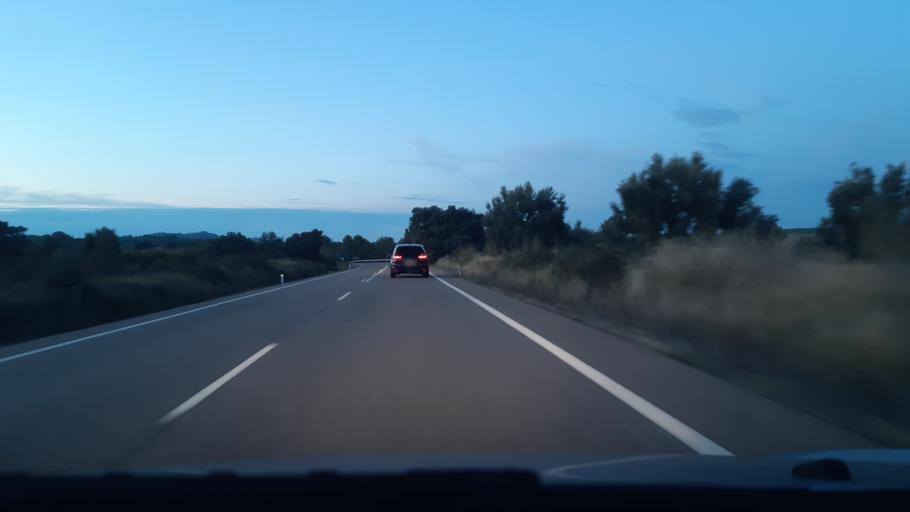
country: ES
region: Aragon
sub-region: Provincia de Teruel
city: Calaceite
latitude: 40.9691
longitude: 0.2081
